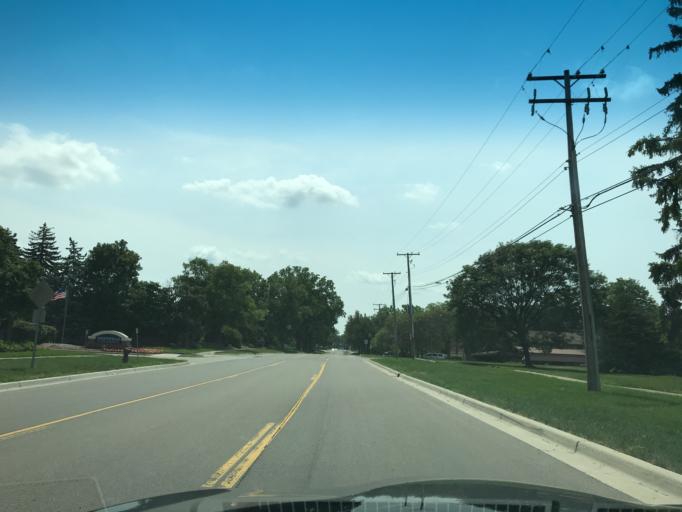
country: US
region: Michigan
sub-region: Oakland County
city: Bingham Farms
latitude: 42.4838
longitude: -83.2795
